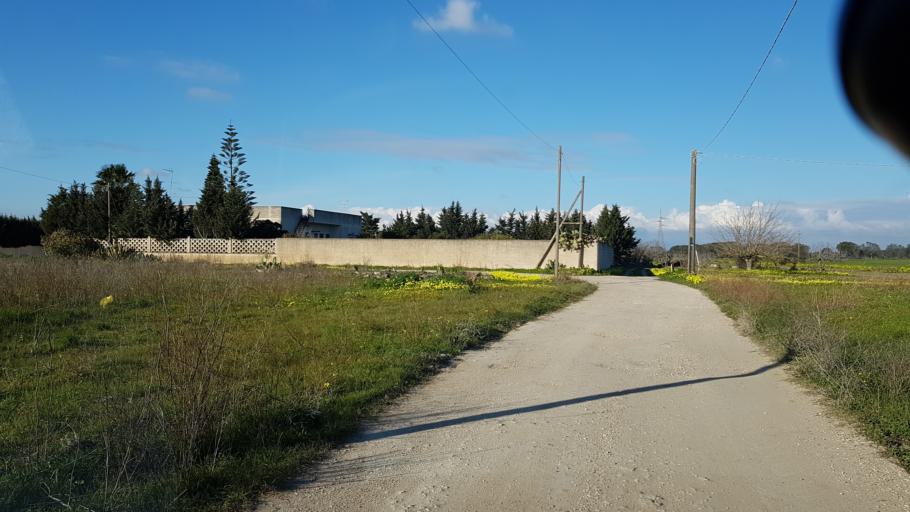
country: IT
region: Apulia
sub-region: Provincia di Brindisi
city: Tuturano
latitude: 40.5435
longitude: 17.9587
